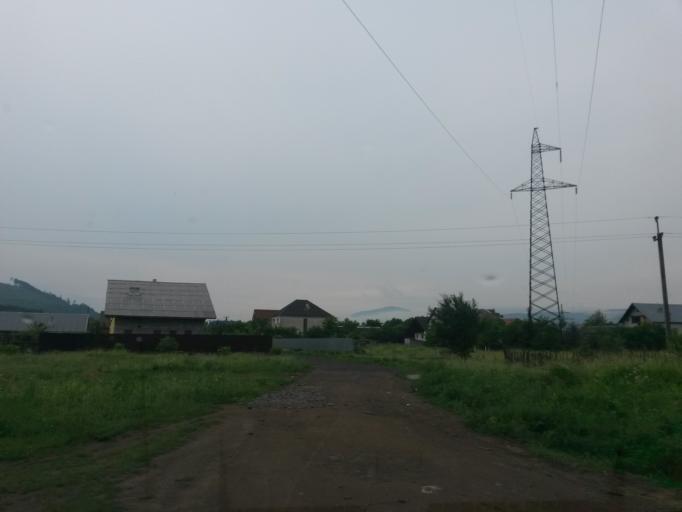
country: UA
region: Zakarpattia
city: Velykyi Bereznyi
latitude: 48.9063
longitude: 22.4654
